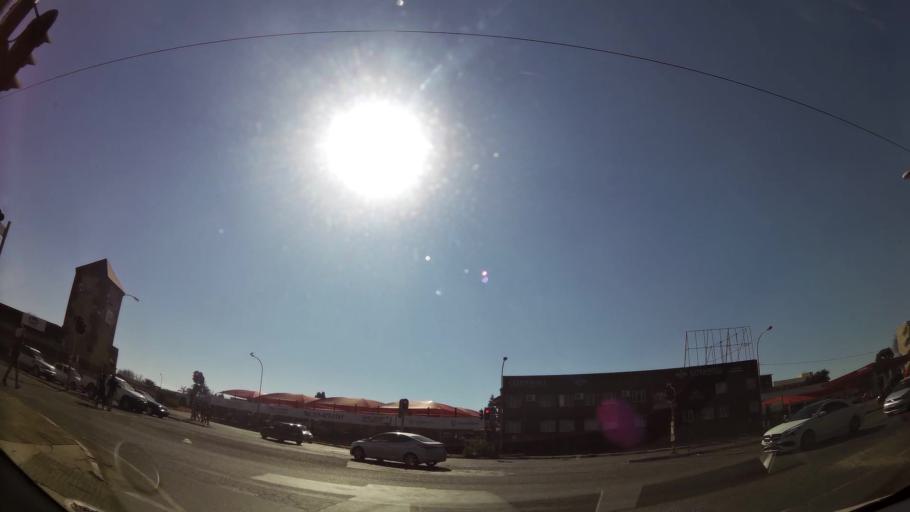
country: ZA
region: Gauteng
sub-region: City of Johannesburg Metropolitan Municipality
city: Johannesburg
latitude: -26.1768
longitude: 27.9712
